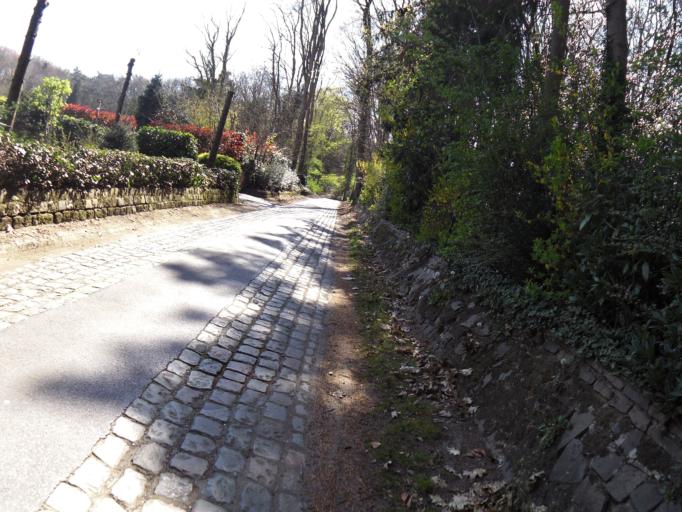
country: BE
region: Flanders
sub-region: Provincie Oost-Vlaanderen
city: Sint-Martens-Latem
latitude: 51.0155
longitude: 3.6276
